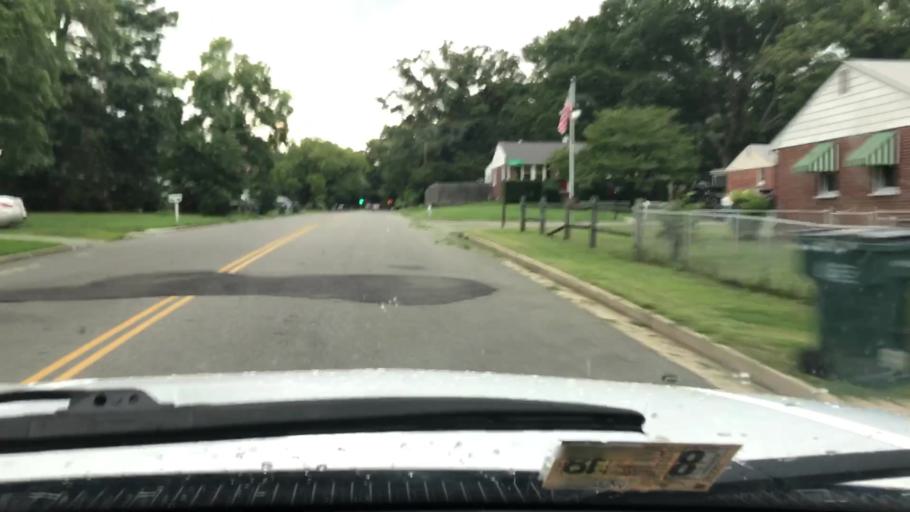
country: US
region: Virginia
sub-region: Henrico County
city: Dumbarton
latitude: 37.5977
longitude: -77.5090
